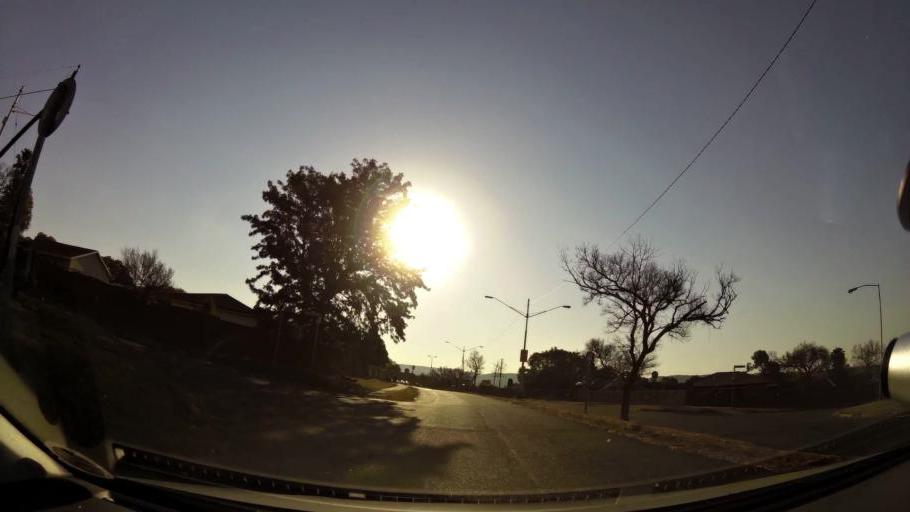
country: ZA
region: Gauteng
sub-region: City of Tshwane Metropolitan Municipality
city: Pretoria
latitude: -25.7555
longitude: 28.1293
